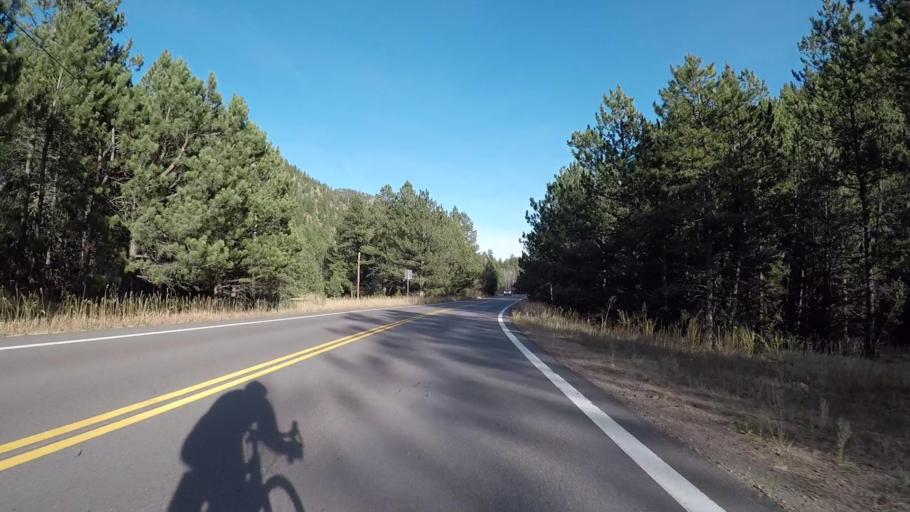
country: US
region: Colorado
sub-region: Boulder County
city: Nederland
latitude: 40.0748
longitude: -105.4190
